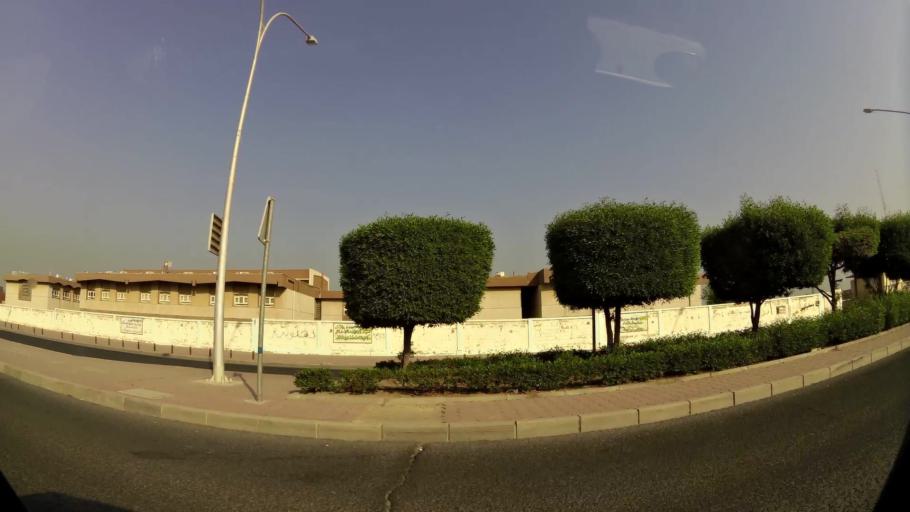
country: KW
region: Al Ahmadi
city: Al Manqaf
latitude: 29.1130
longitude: 48.1055
